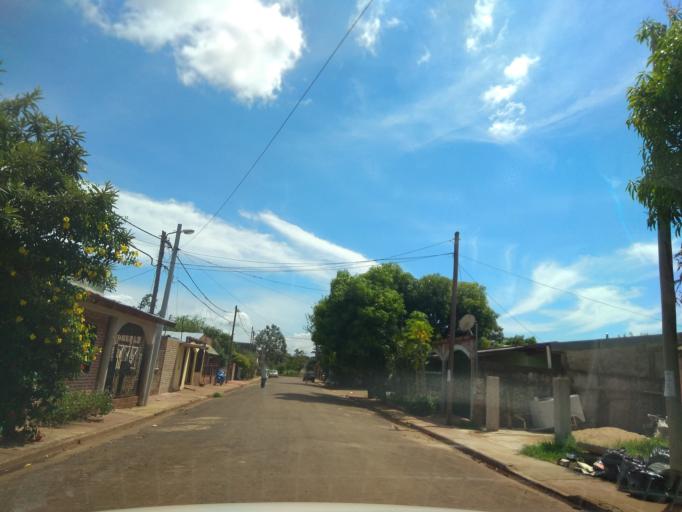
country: AR
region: Misiones
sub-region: Departamento de Capital
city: Posadas
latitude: -27.3861
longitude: -55.9261
